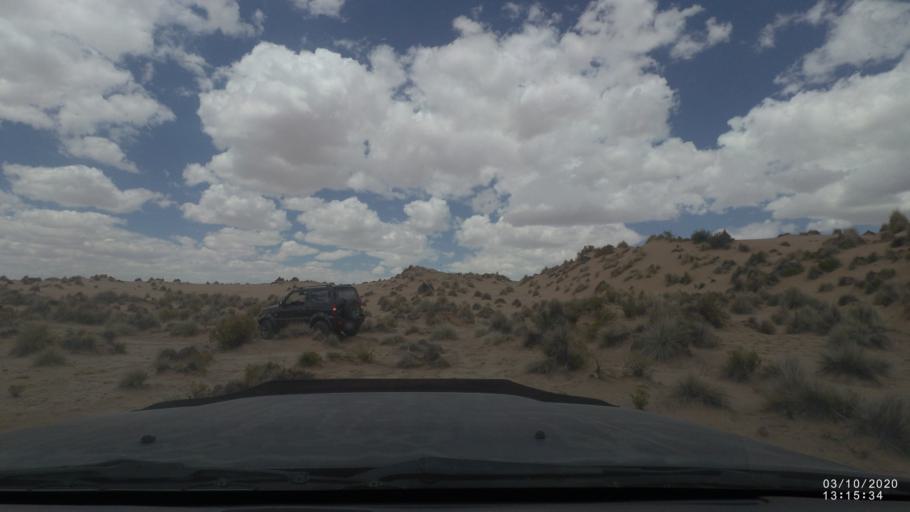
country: BO
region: Oruro
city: Poopo
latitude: -18.6912
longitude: -67.5338
